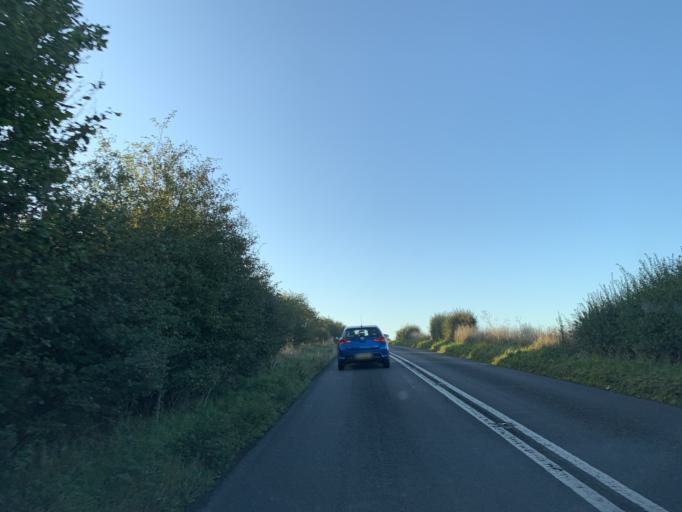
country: GB
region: England
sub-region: Wiltshire
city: Woodford
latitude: 51.1359
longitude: -1.8578
